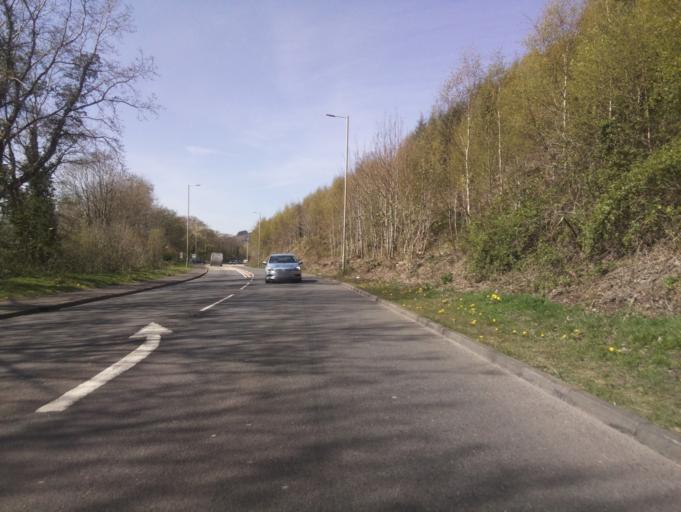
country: GB
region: Wales
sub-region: Merthyr Tydfil County Borough
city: Treharris
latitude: 51.6558
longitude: -3.3341
